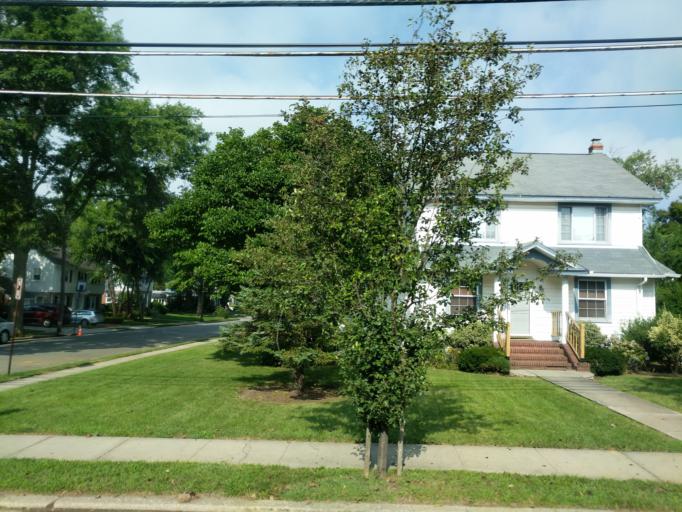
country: US
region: New York
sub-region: Nassau County
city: Malverne
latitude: 40.6726
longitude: -73.6702
